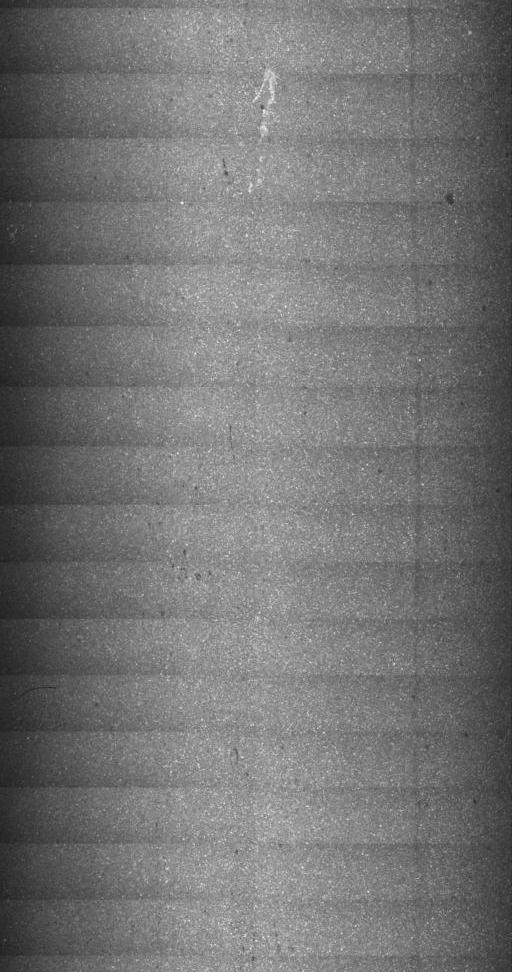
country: US
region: Vermont
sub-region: Lamoille County
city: Johnson
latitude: 44.5548
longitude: -72.7960
